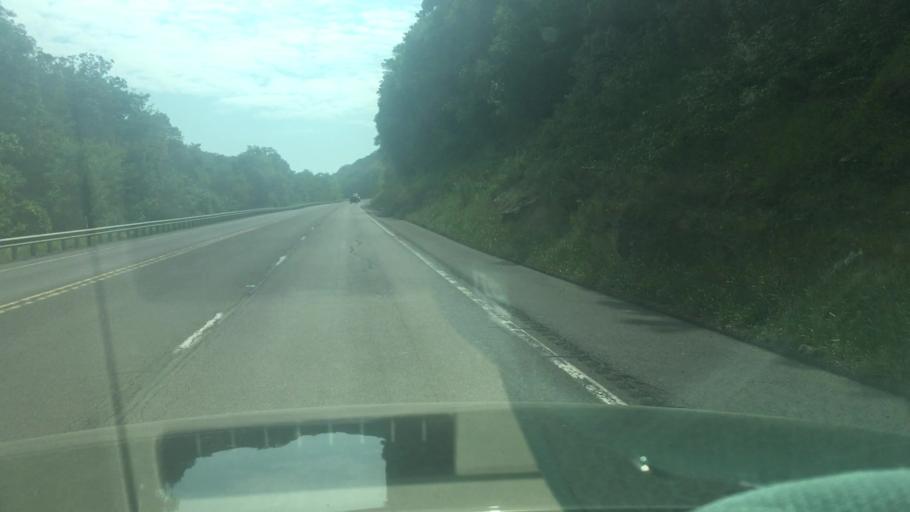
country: US
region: Pennsylvania
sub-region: Northumberland County
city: Kulpmont
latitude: 40.8205
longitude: -76.4815
